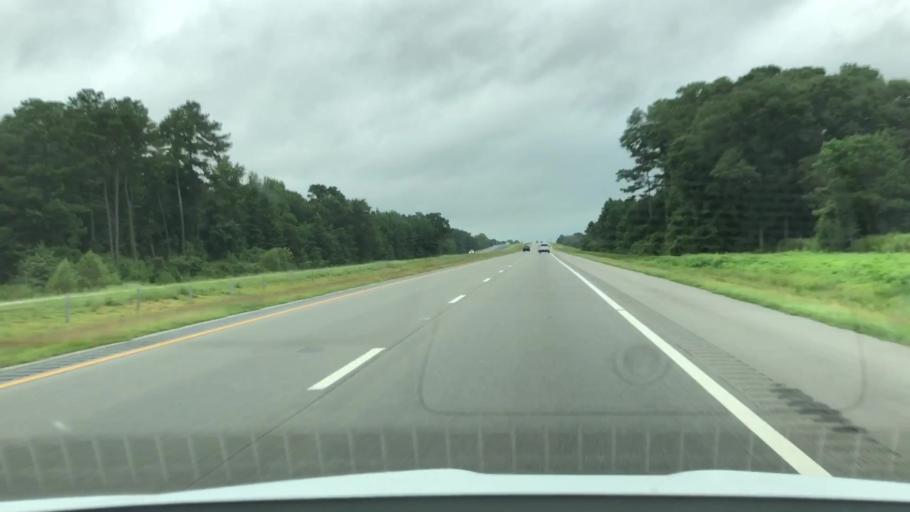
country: US
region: North Carolina
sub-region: Lenoir County
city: La Grange
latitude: 35.3357
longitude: -77.8435
